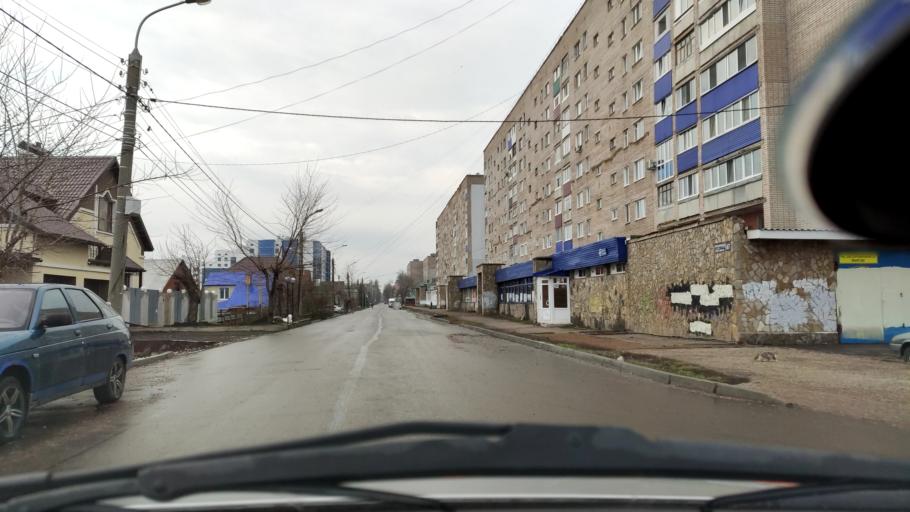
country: RU
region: Bashkortostan
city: Sterlitamak
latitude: 53.6242
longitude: 55.9560
